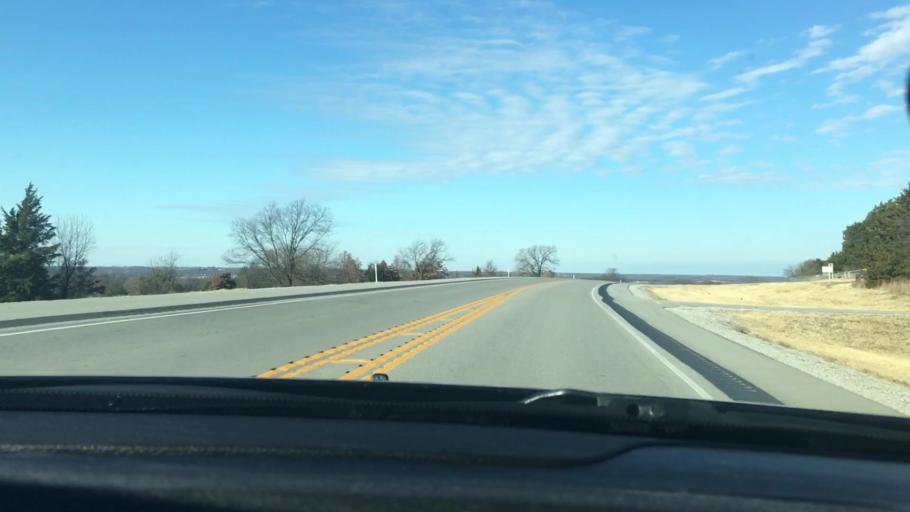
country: US
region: Oklahoma
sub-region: Love County
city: Marietta
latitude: 33.9382
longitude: -97.2665
